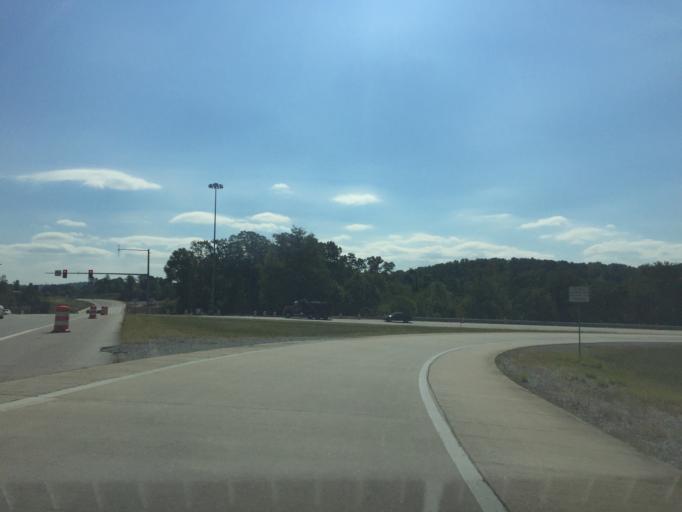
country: US
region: Tennessee
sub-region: Hamilton County
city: Harrison
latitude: 35.0735
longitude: -85.1109
